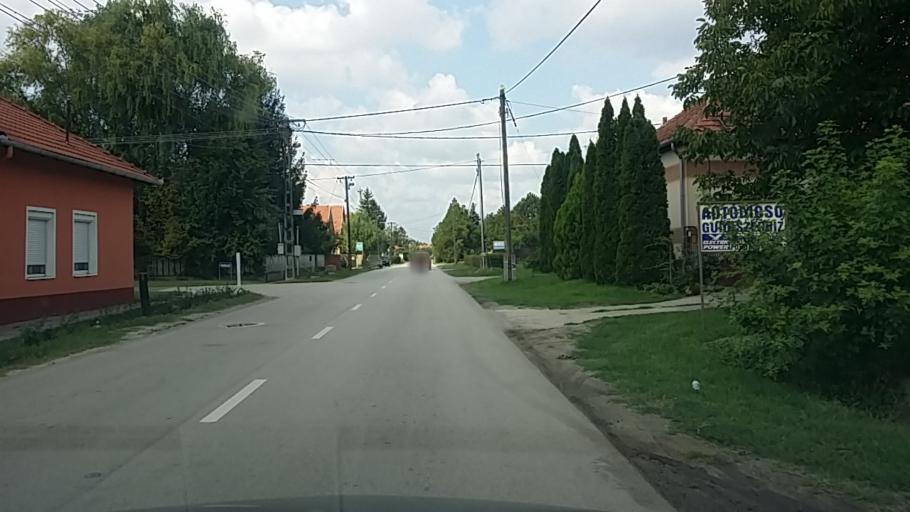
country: HU
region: Bacs-Kiskun
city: Tiszaalpar
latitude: 46.8095
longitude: 20.0032
